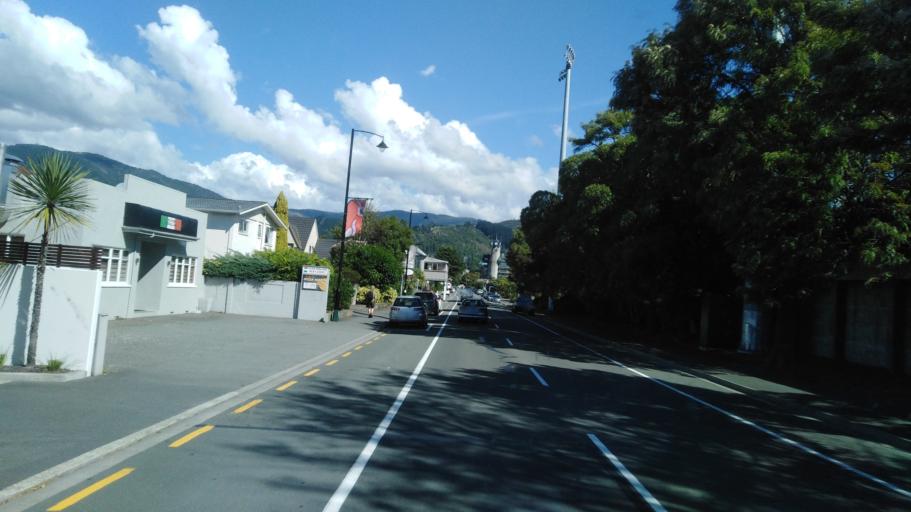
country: NZ
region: Nelson
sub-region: Nelson City
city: Nelson
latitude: -41.2664
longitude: 173.2842
